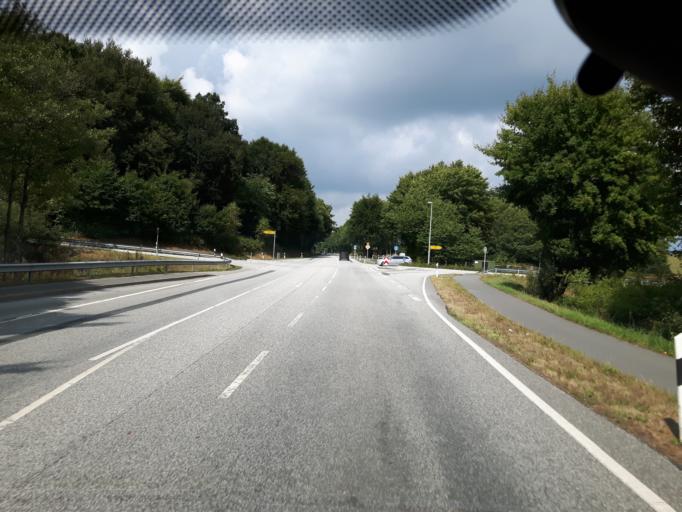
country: DE
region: Schleswig-Holstein
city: Holzbunge
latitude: 54.3577
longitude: 9.7044
